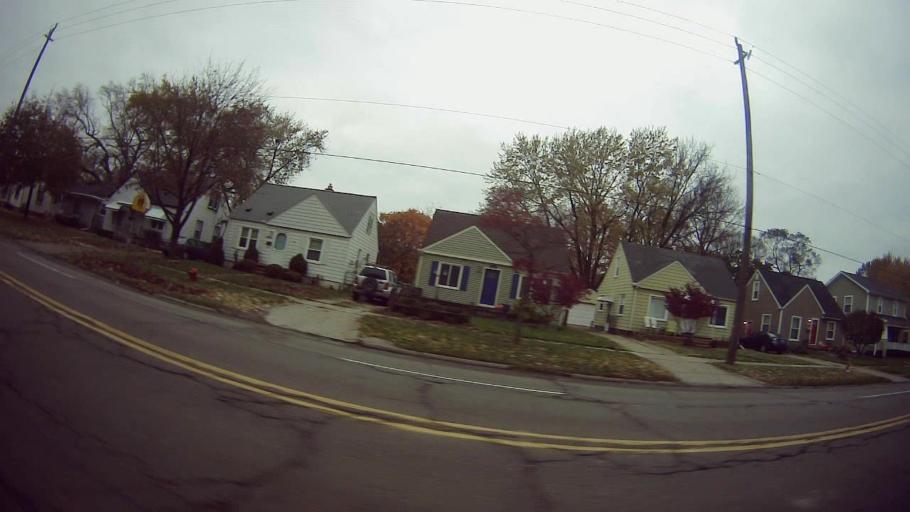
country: US
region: Michigan
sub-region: Oakland County
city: Madison Heights
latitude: 42.4817
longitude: -83.1239
